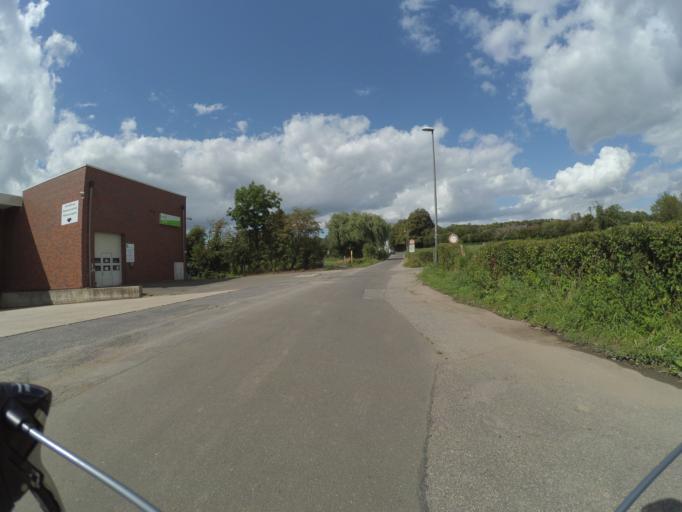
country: DE
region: North Rhine-Westphalia
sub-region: Regierungsbezirk Koln
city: Aachen
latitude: 50.8018
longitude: 6.0936
